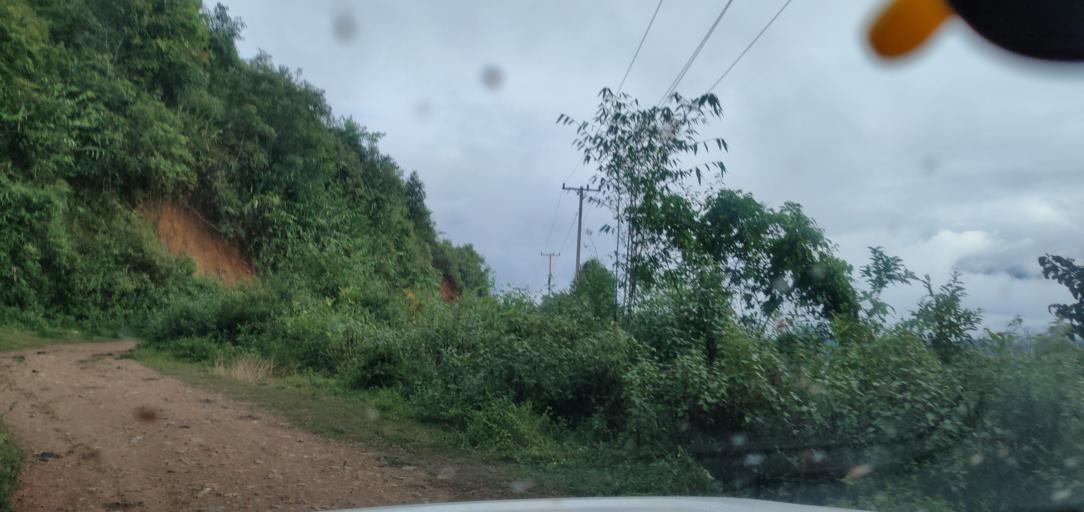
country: LA
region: Phongsali
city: Phongsali
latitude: 21.4458
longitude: 102.2930
